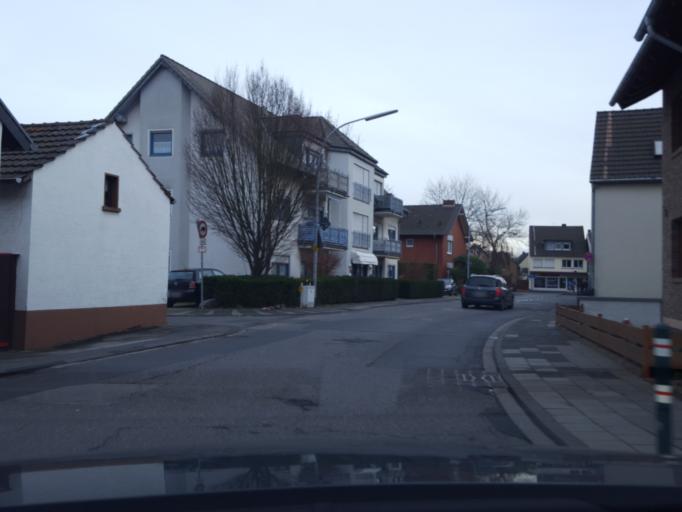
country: DE
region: North Rhine-Westphalia
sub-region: Regierungsbezirk Koln
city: Bonn
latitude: 50.7760
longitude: 7.0706
